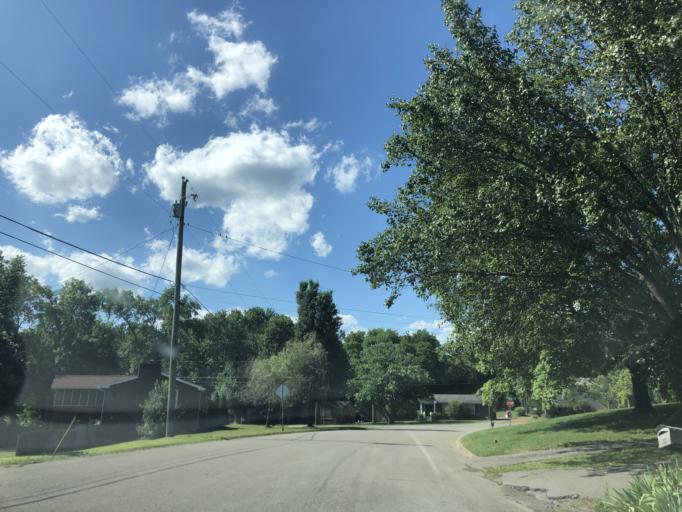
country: US
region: Tennessee
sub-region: Davidson County
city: Belle Meade
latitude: 36.0600
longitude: -86.9277
